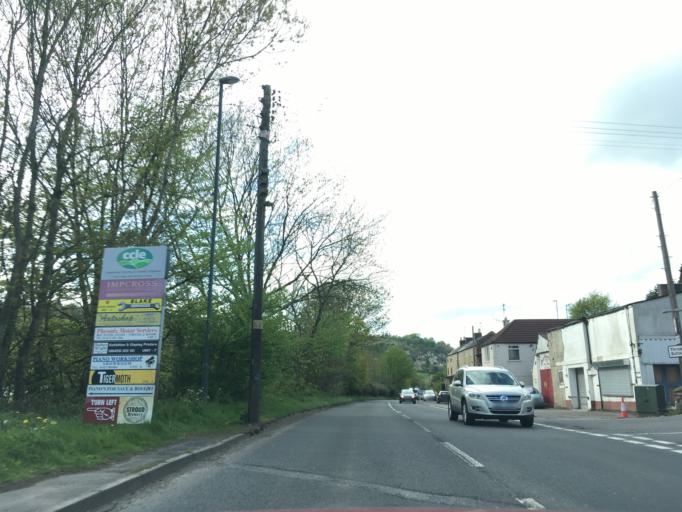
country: GB
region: England
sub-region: Gloucestershire
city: Brimscombe
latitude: 51.7245
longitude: -2.1990
